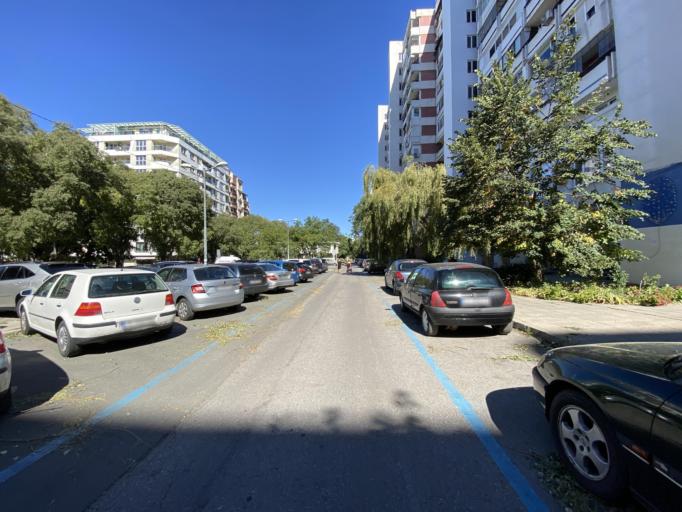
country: BG
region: Burgas
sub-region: Obshtina Burgas
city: Burgas
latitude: 42.5043
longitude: 27.4676
